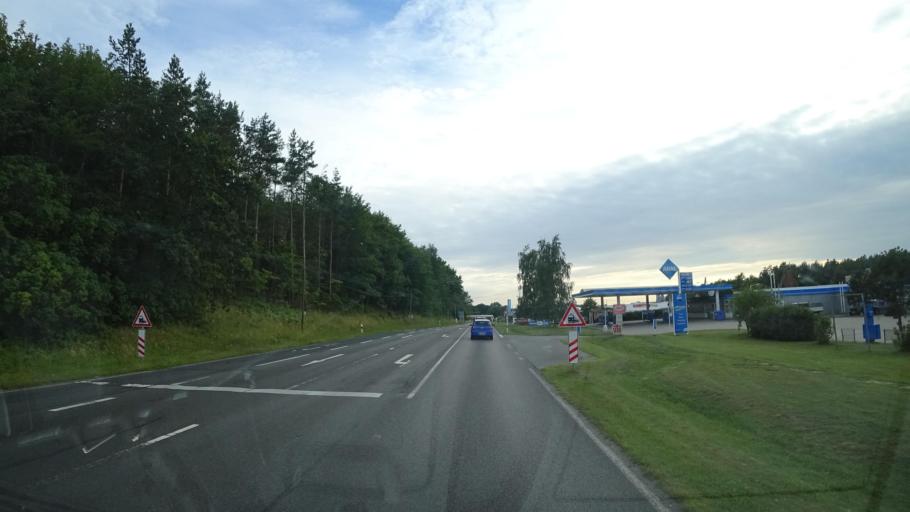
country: DE
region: Mecklenburg-Vorpommern
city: Bergen auf Ruegen
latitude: 54.4071
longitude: 13.4191
